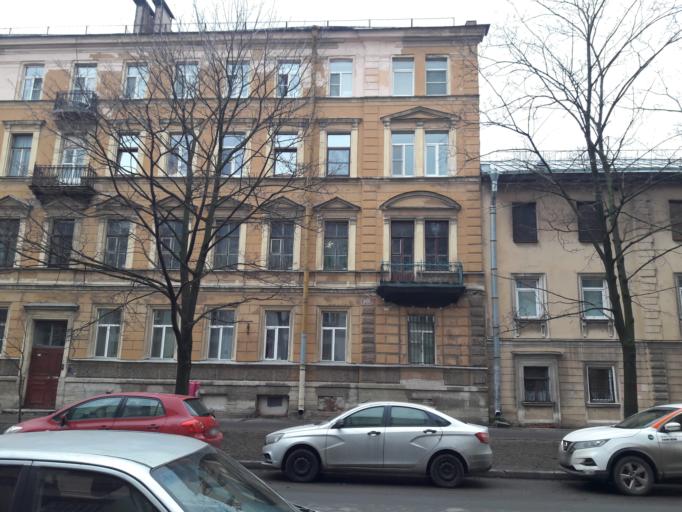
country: RU
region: St.-Petersburg
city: Admiralteisky
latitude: 59.9224
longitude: 30.2888
